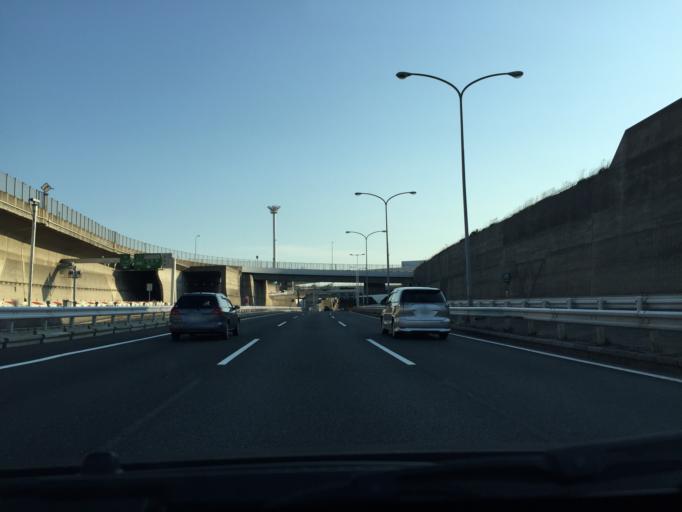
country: JP
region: Kanagawa
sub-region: Kawasaki-shi
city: Kawasaki
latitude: 35.5157
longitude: 139.7899
